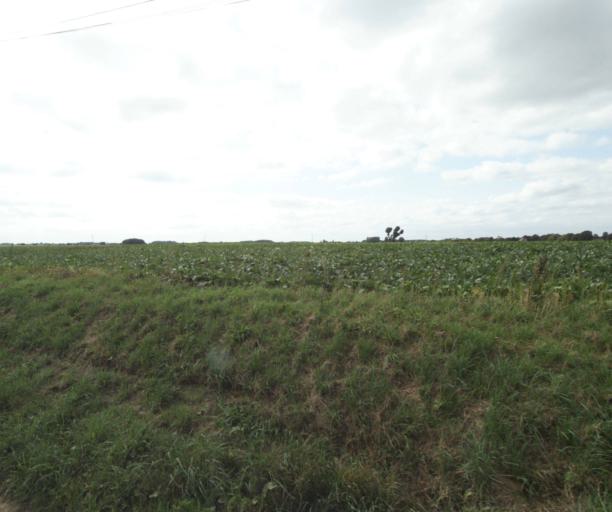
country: FR
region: Nord-Pas-de-Calais
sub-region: Departement du Nord
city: Baisieux
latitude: 50.6059
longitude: 3.2426
